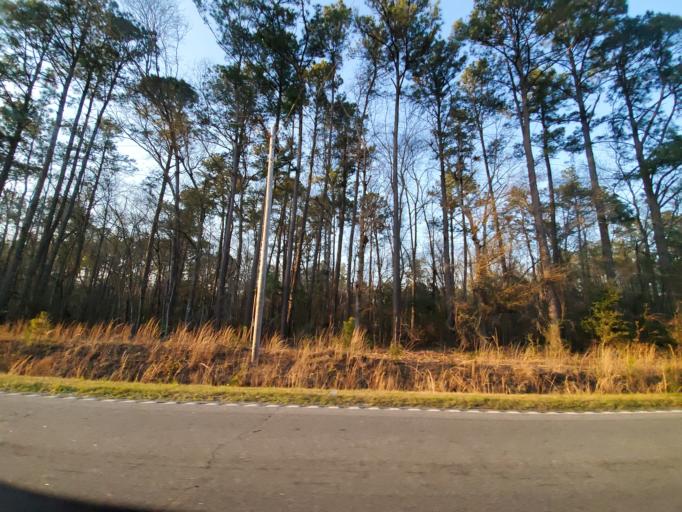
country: US
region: South Carolina
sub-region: Dorchester County
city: Saint George
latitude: 33.0499
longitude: -80.5104
